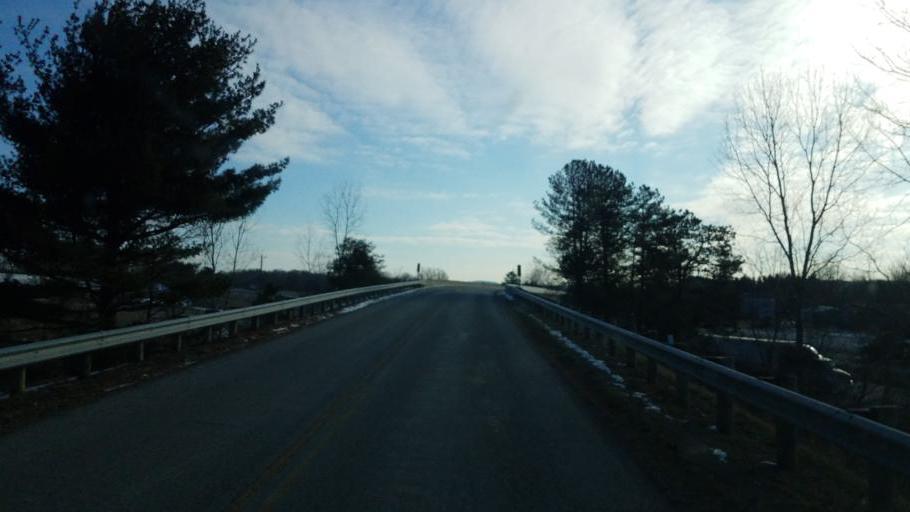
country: US
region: Ohio
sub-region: Richland County
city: Lexington
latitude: 40.6185
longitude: -82.5728
